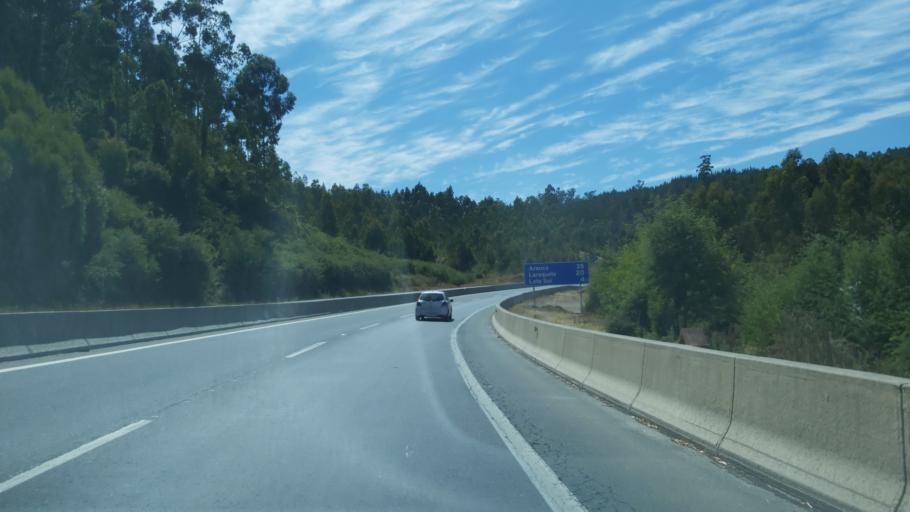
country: CL
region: Biobio
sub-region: Provincia de Concepcion
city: Lota
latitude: -37.0720
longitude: -73.1394
